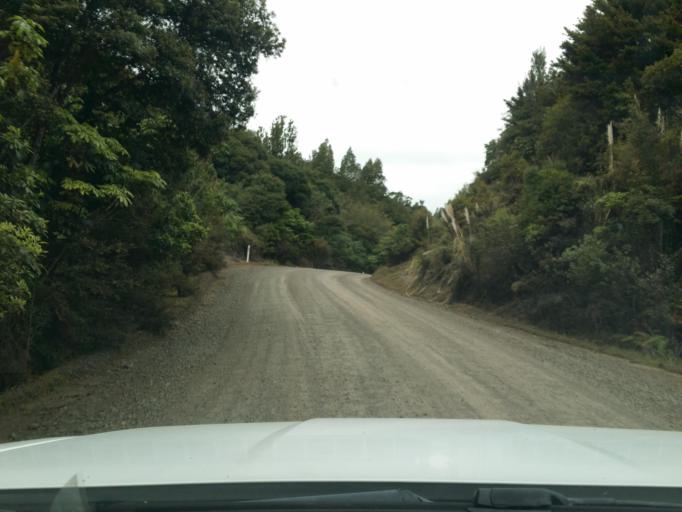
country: NZ
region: Northland
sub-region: Kaipara District
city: Dargaville
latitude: -35.7148
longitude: 173.6388
